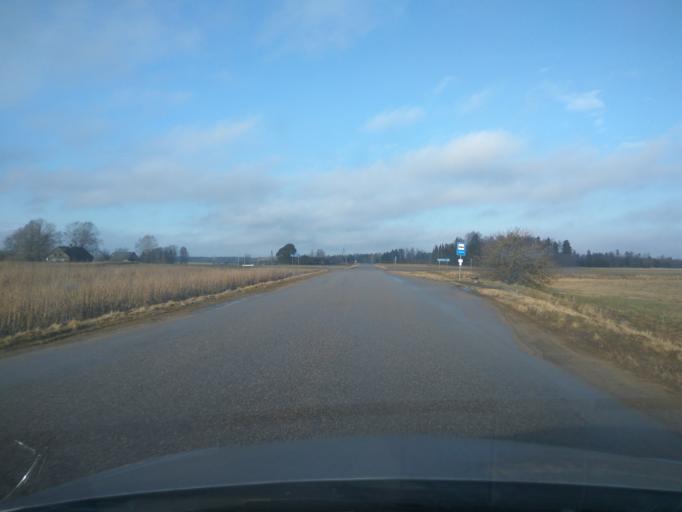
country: LV
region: Saldus Rajons
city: Saldus
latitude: 56.8223
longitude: 22.3773
